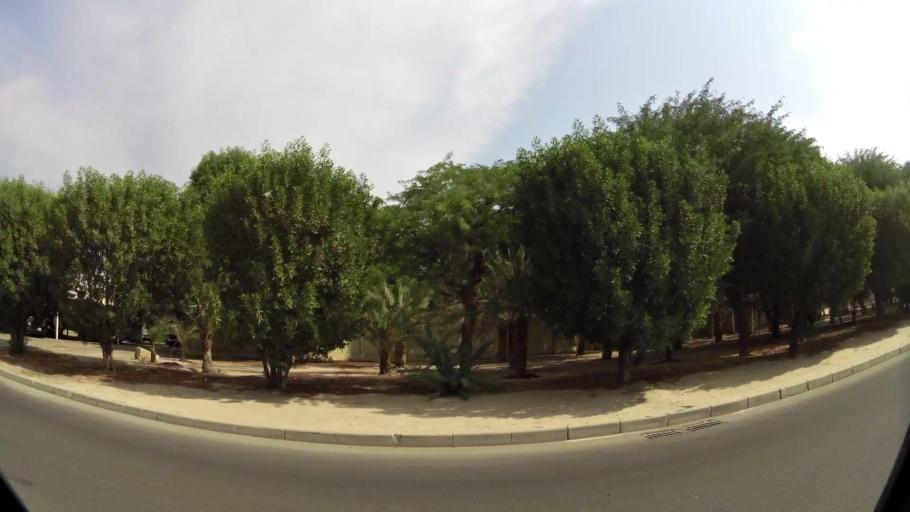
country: KW
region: Al Asimah
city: Ash Shamiyah
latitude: 29.3493
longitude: 47.9752
